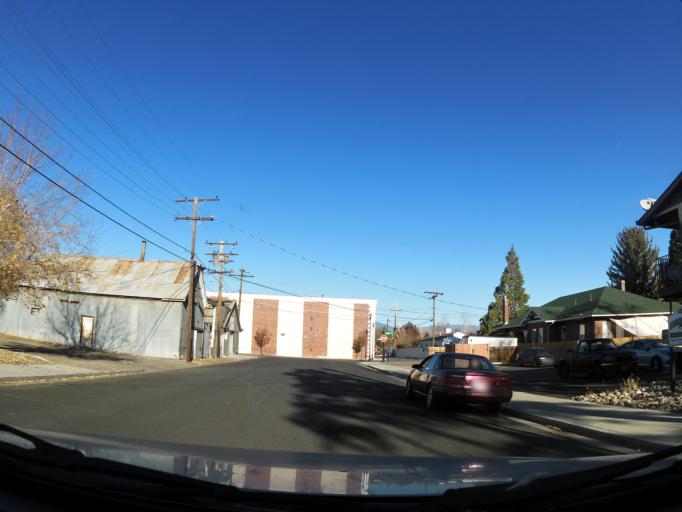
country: US
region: Nevada
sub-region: Douglas County
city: Gardnerville
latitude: 38.9408
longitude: -119.7473
